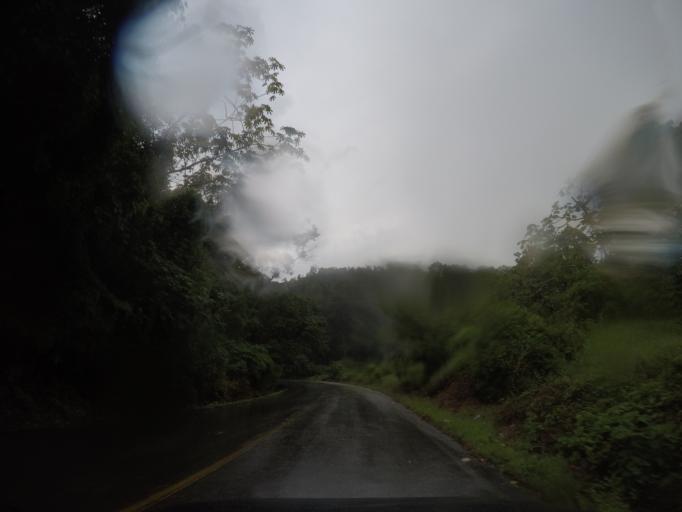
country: MX
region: Oaxaca
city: San Gabriel Mixtepec
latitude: 16.0680
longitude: -97.0753
